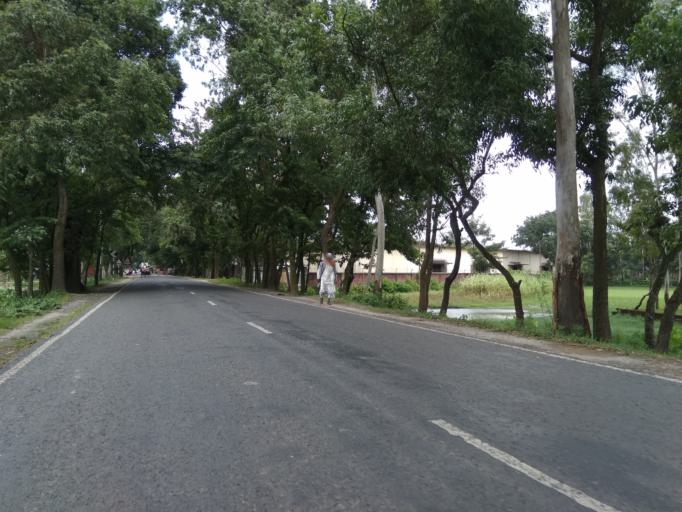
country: BD
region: Rajshahi
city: Saidpur
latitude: 25.7728
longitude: 88.7966
